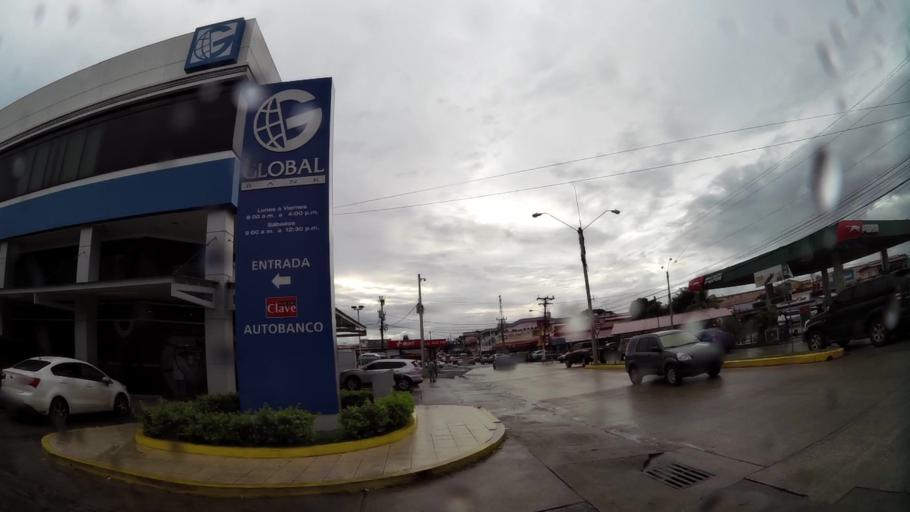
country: PA
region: Veraguas
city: Santiago de Veraguas
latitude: 8.0975
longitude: -80.9766
